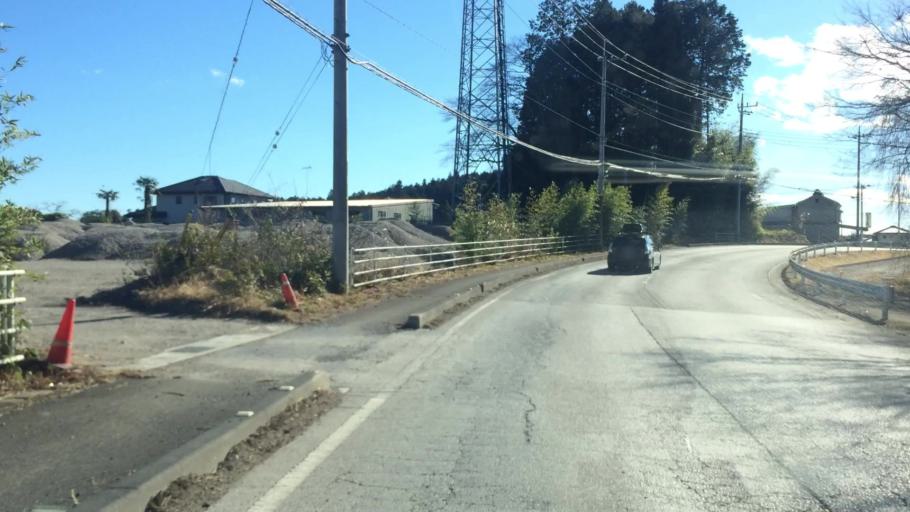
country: JP
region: Tochigi
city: Imaichi
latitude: 36.7270
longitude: 139.7496
